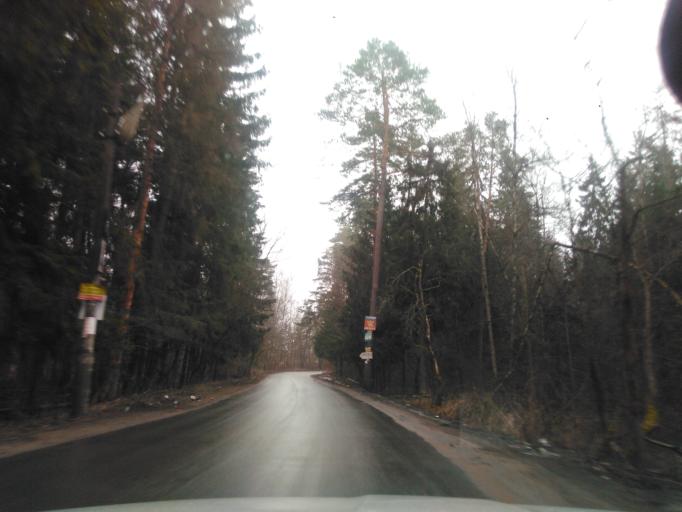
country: RU
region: Moskovskaya
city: Andreyevka
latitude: 55.9350
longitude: 37.1424
